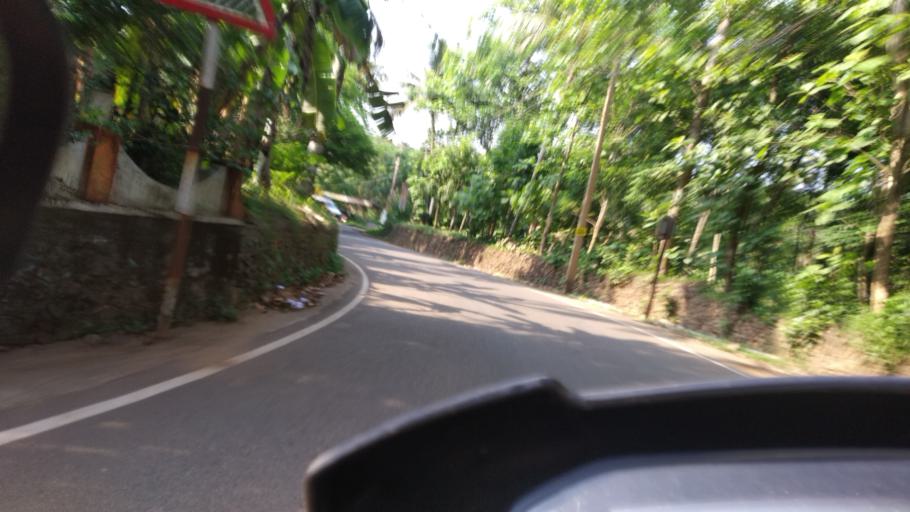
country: IN
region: Kerala
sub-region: Ernakulam
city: Piravam
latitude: 9.8598
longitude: 76.5187
